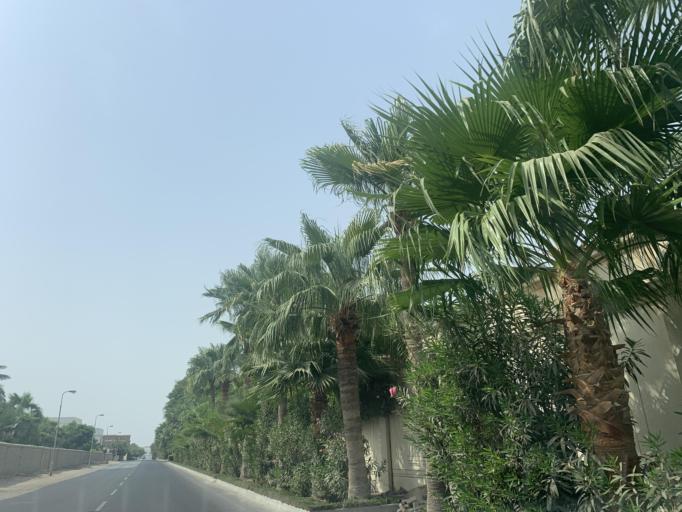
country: BH
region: Manama
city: Jidd Hafs
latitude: 26.2050
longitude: 50.4713
